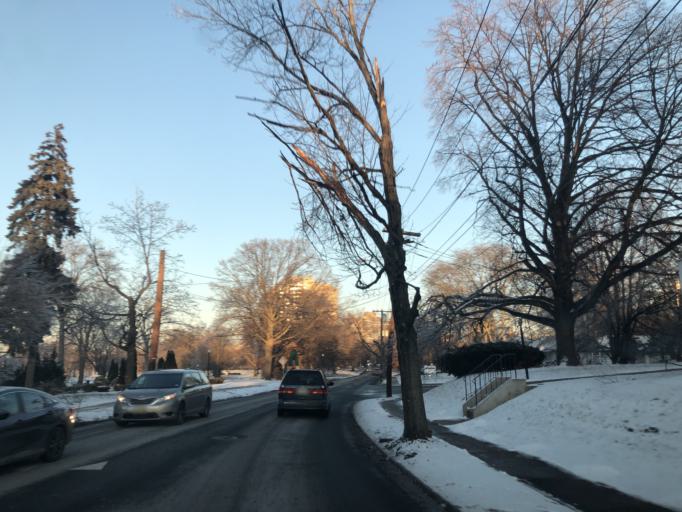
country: US
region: New Jersey
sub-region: Essex County
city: Orange
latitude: 40.7557
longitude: -74.2355
